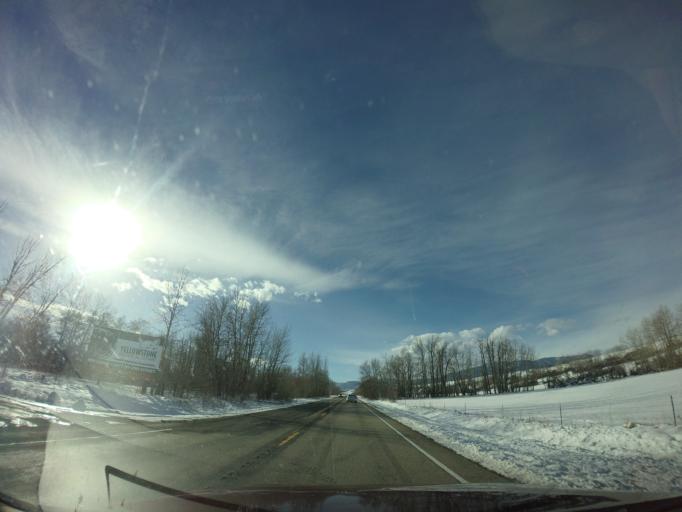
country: US
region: Montana
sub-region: Carbon County
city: Red Lodge
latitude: 45.2553
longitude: -109.2304
